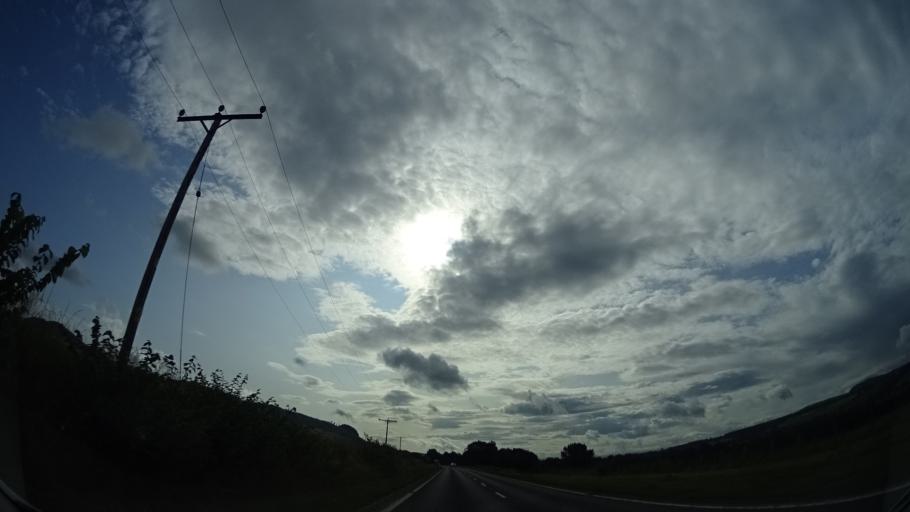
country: GB
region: Scotland
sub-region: Highland
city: Muir of Ord
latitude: 57.5616
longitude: -4.5661
